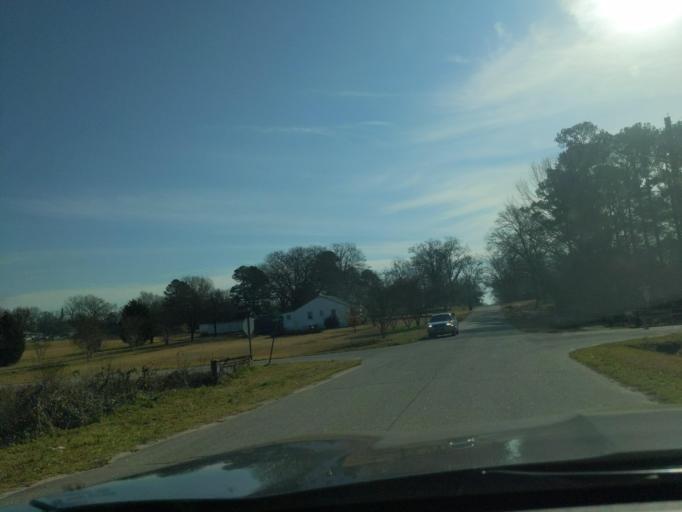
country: US
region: South Carolina
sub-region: Abbeville County
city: Calhoun Falls
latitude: 34.0924
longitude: -82.5938
